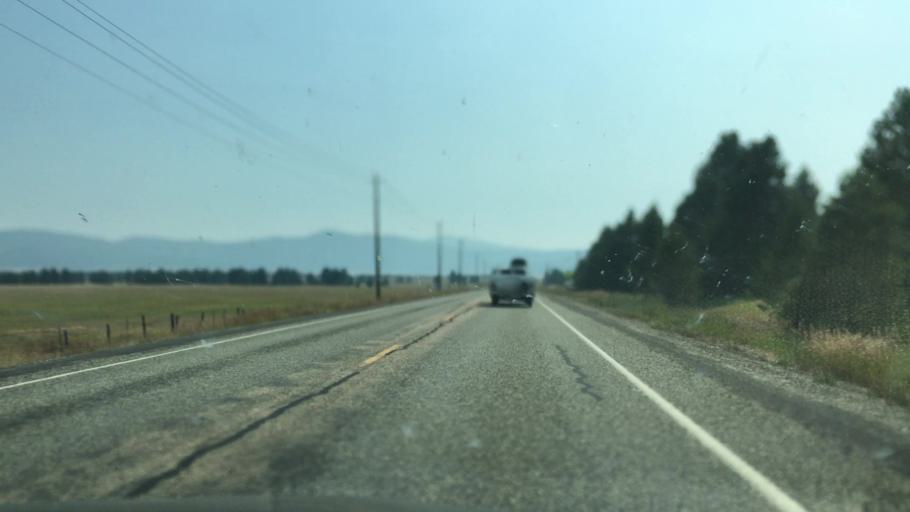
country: US
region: Idaho
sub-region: Valley County
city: Cascade
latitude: 44.3612
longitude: -116.0207
